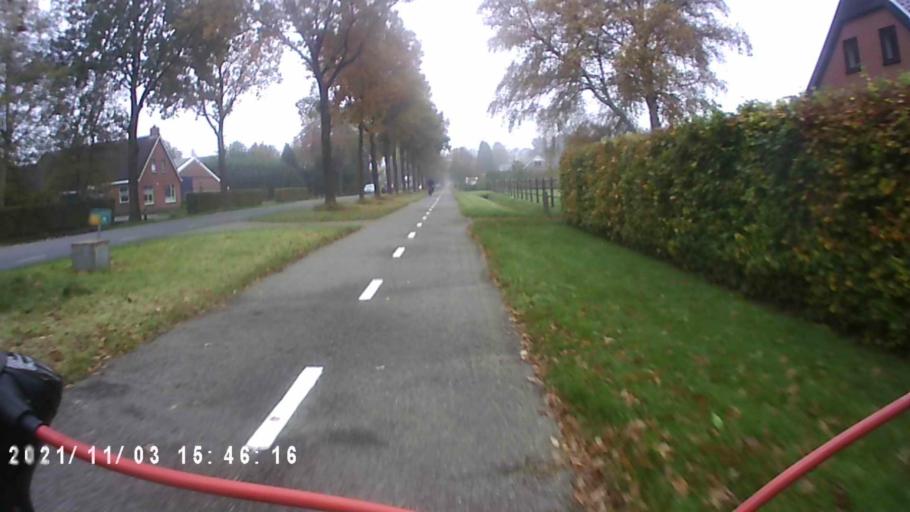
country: NL
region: Groningen
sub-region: Gemeente Leek
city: Leek
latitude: 53.0942
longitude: 6.3410
